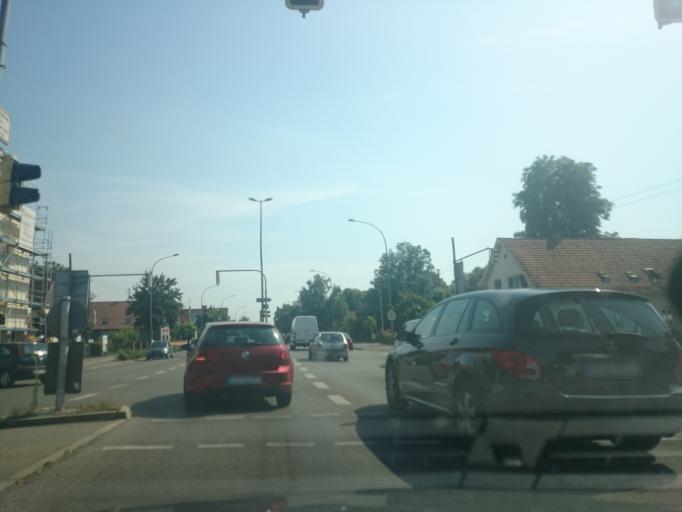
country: DE
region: Bavaria
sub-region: Swabia
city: Konigsbrunn
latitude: 48.2813
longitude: 10.8931
